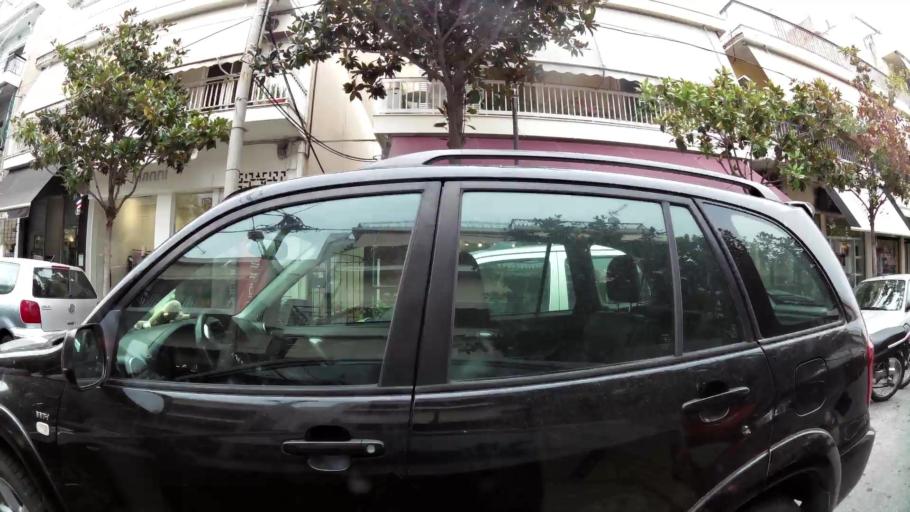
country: GR
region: Attica
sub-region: Nomarchia Athinas
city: Aigaleo
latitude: 37.9936
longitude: 23.6822
